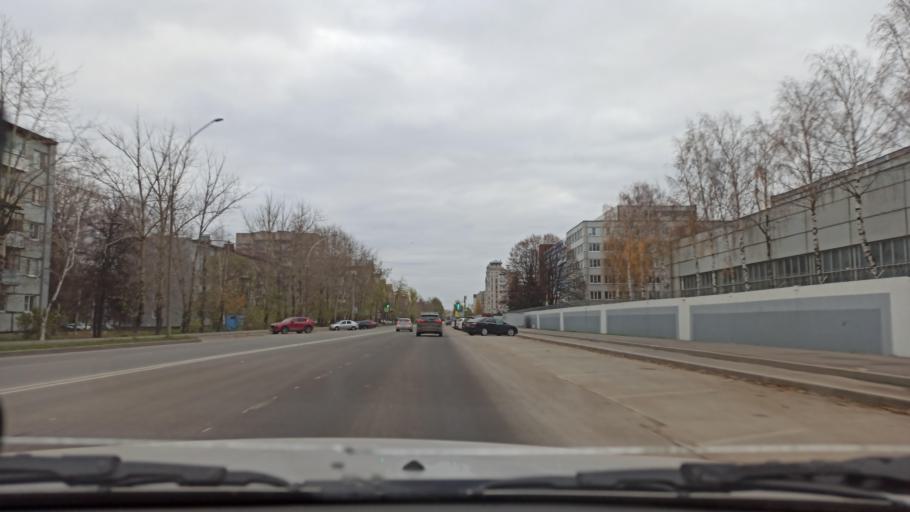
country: RU
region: Vologda
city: Vologda
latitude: 59.2170
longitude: 39.8684
